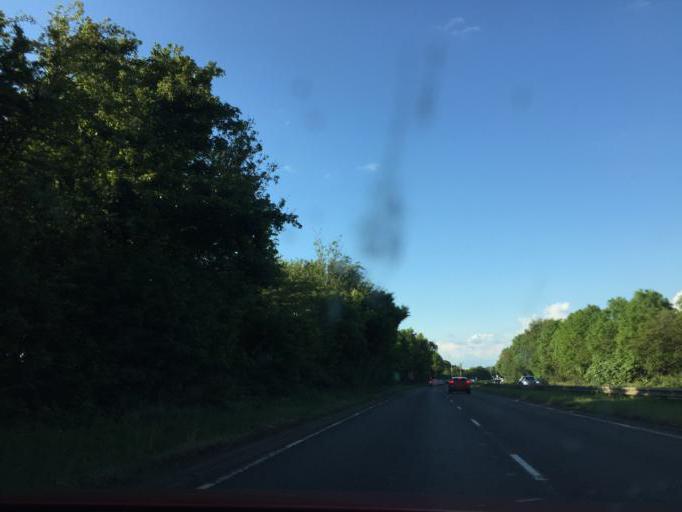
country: GB
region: England
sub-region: Warwickshire
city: Bedworth
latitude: 52.4911
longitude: -1.4824
